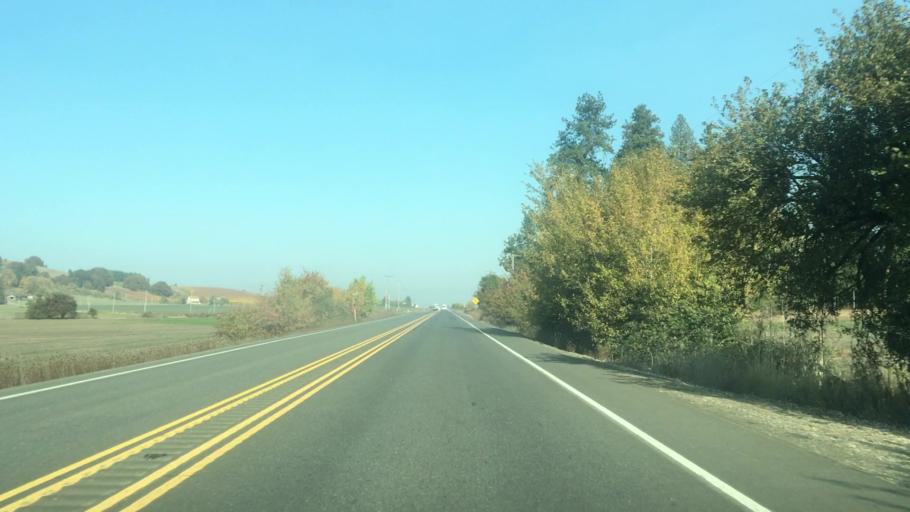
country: US
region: Oregon
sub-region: Yamhill County
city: Amity
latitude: 45.1288
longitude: -123.3006
